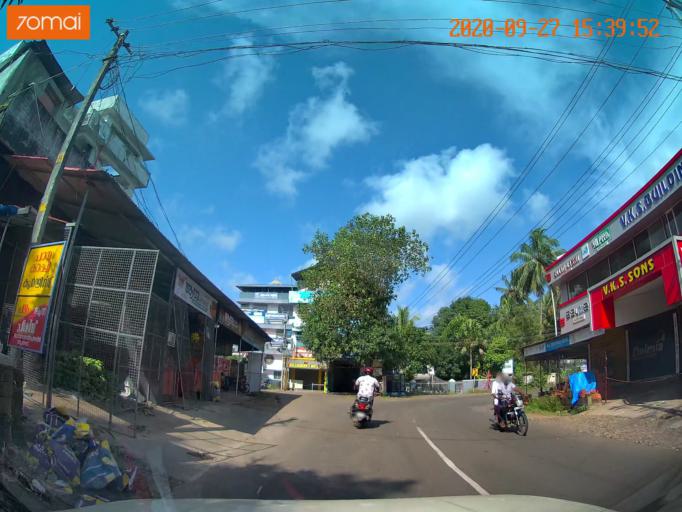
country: IN
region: Kerala
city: Chavakkad
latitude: 10.4697
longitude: 76.0836
